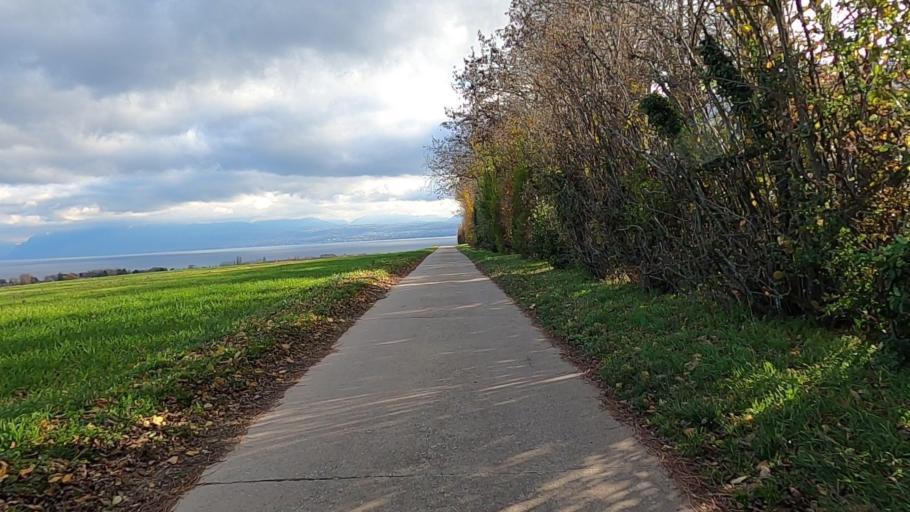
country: CH
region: Vaud
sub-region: Morges District
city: Saint-Prex
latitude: 46.5104
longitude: 6.4576
